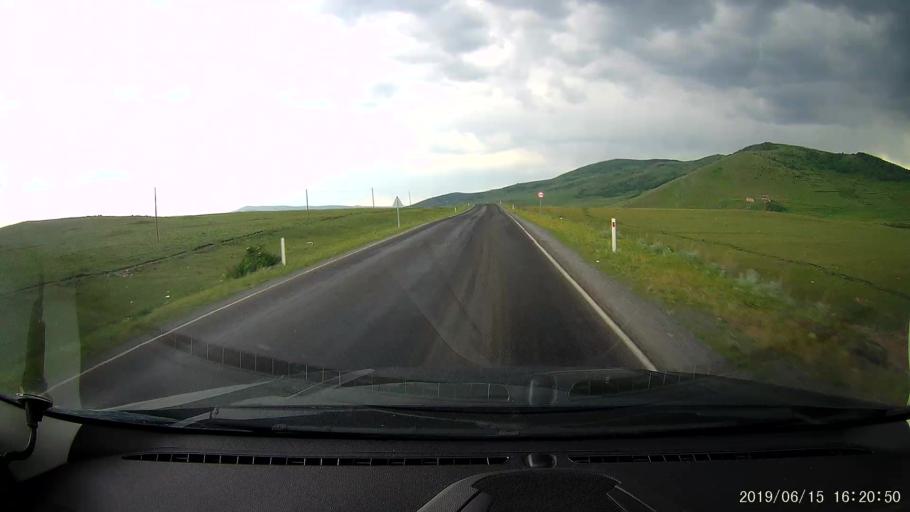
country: TR
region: Ardahan
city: Hanak
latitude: 41.2071
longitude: 42.8464
